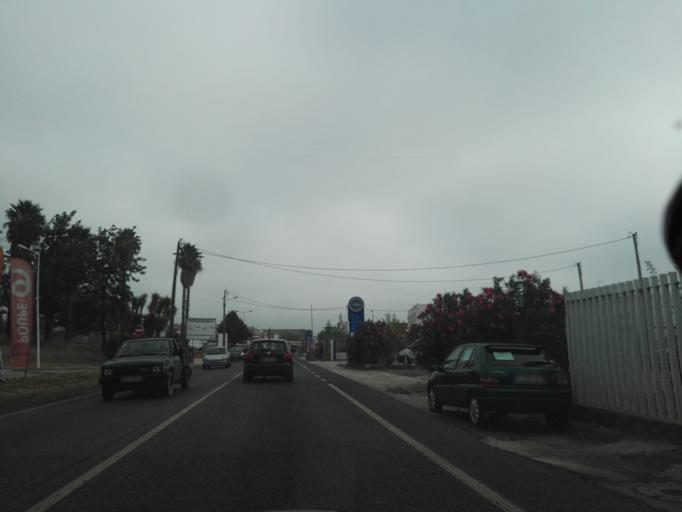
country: PT
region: Lisbon
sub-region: Vila Franca de Xira
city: Sobralinho
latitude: 38.9064
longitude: -9.0324
